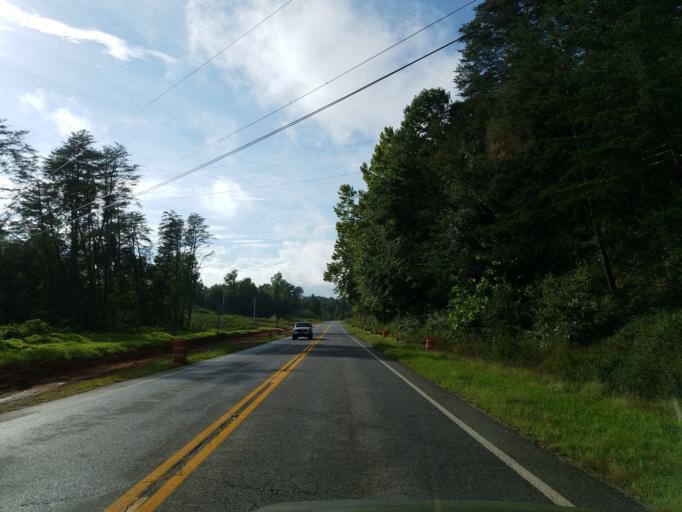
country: US
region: Georgia
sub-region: White County
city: Cleveland
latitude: 34.6095
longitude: -83.7731
